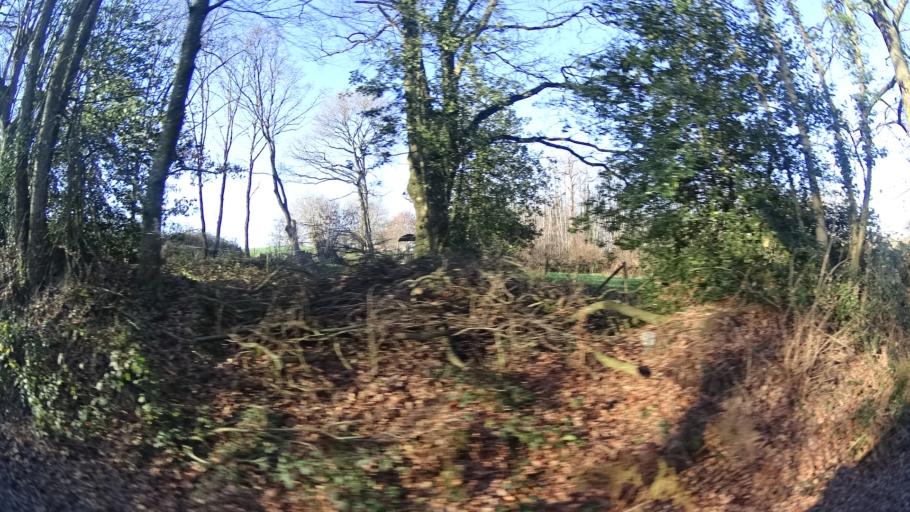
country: FR
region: Brittany
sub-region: Departement du Morbihan
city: Allaire
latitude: 47.6440
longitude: -2.1509
